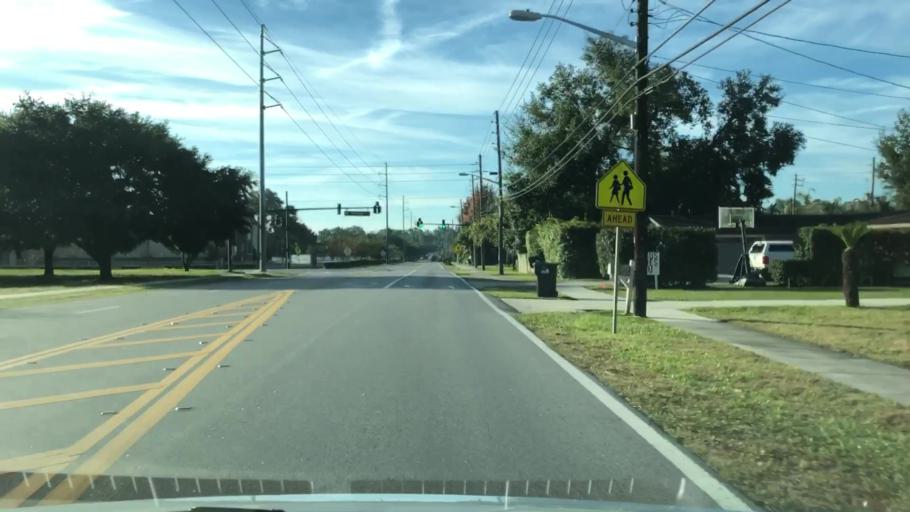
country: US
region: Florida
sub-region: Orange County
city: Conway
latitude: 28.5141
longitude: -81.3393
